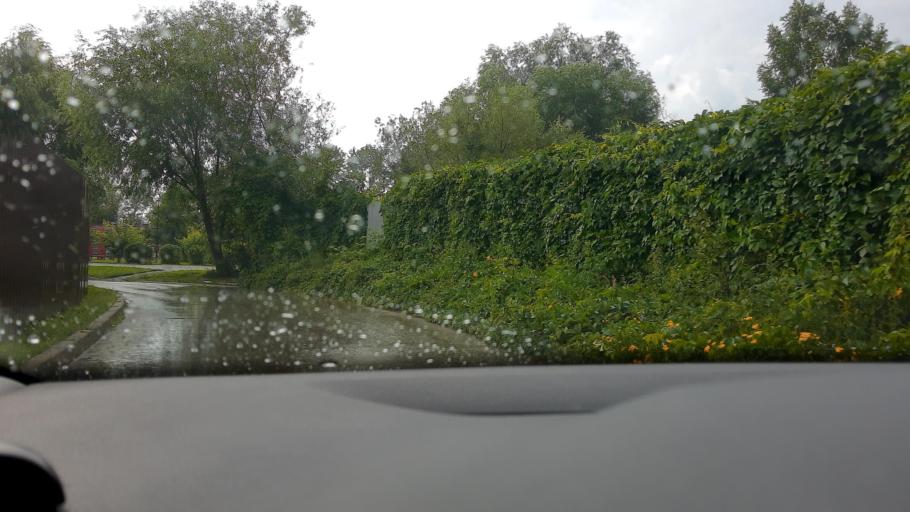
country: RU
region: Moskovskaya
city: Novopodrezkovo
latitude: 55.8829
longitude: 37.3668
